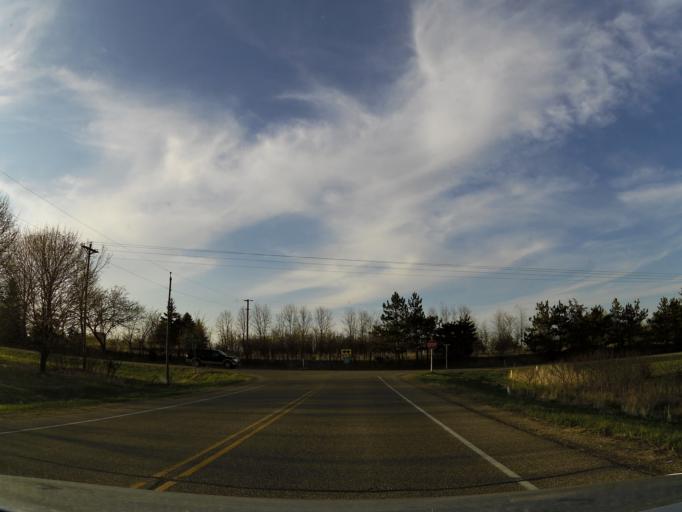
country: US
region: Wisconsin
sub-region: Pierce County
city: River Falls
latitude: 44.9128
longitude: -92.6805
